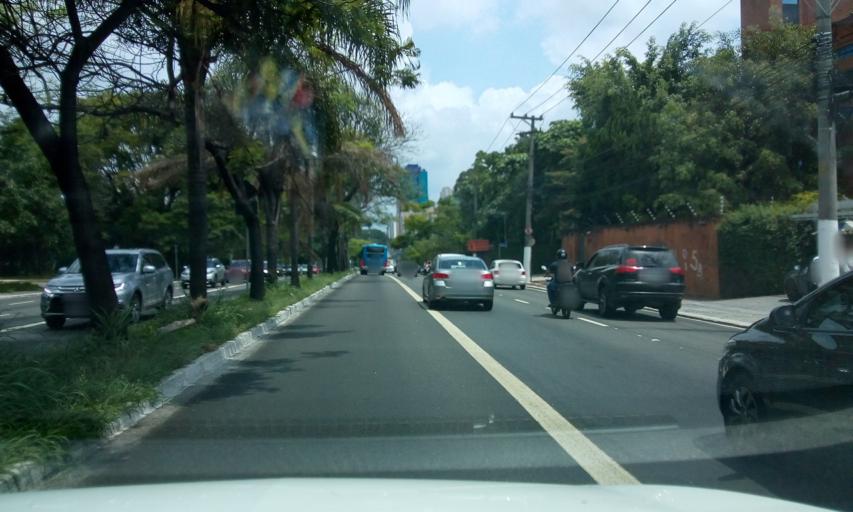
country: BR
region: Sao Paulo
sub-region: Sao Paulo
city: Sao Paulo
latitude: -23.5971
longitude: -46.6563
